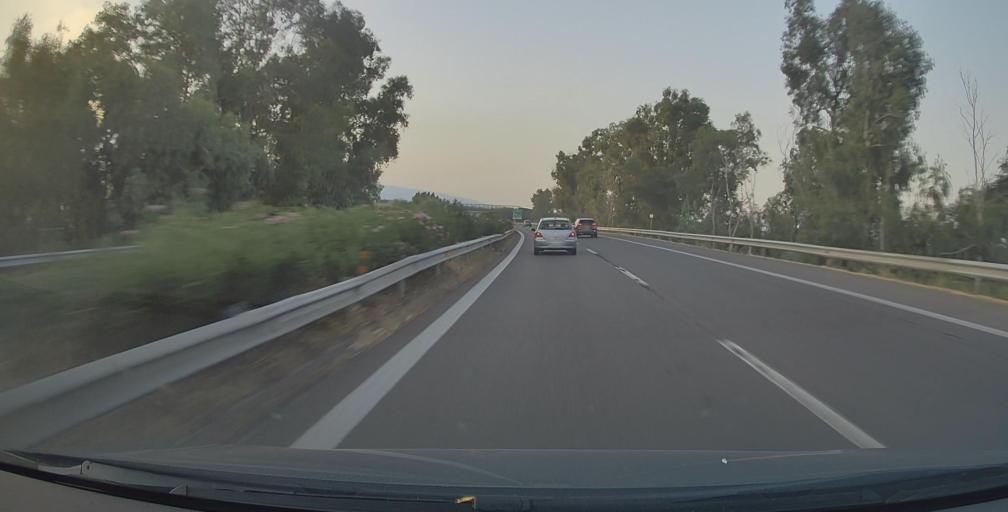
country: IT
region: Sicily
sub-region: Catania
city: Aci Sant'Antonio
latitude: 37.6090
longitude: 15.1345
